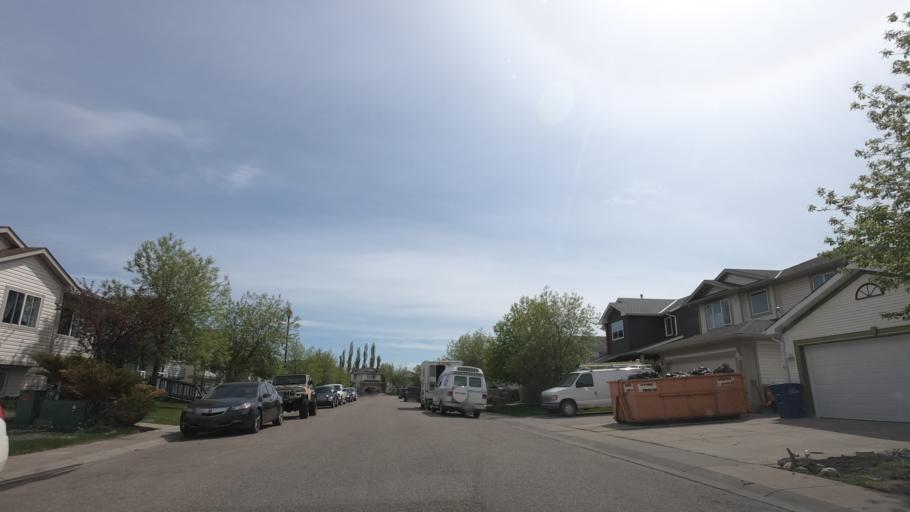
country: CA
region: Alberta
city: Airdrie
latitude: 51.3017
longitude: -114.0208
